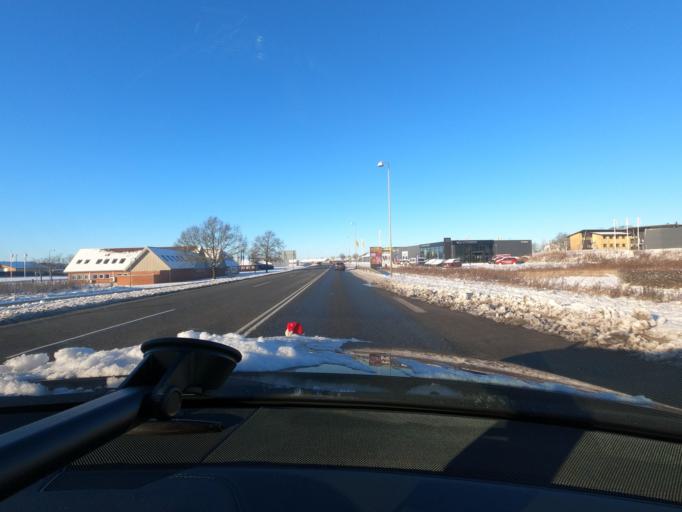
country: DK
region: South Denmark
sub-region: Aabenraa Kommune
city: Rodekro
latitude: 55.0678
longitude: 9.3596
